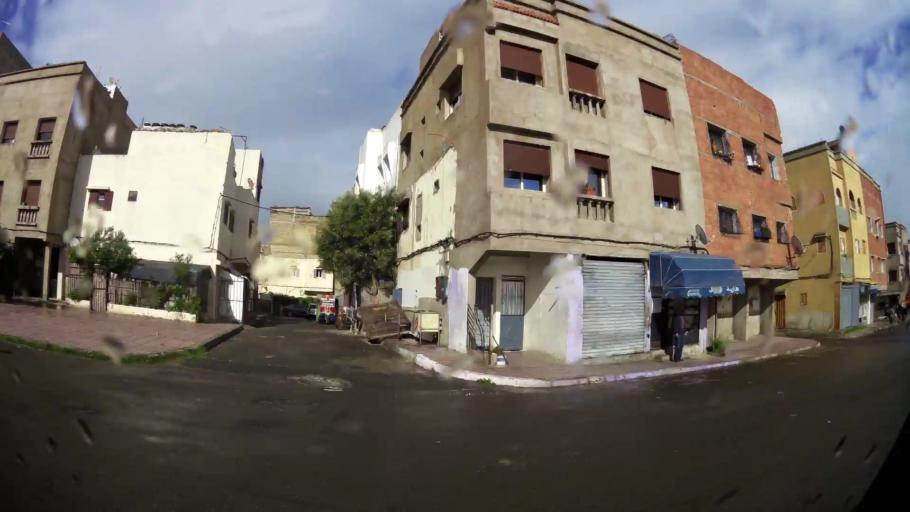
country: MA
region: Grand Casablanca
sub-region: Casablanca
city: Casablanca
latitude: 33.5622
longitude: -7.6941
